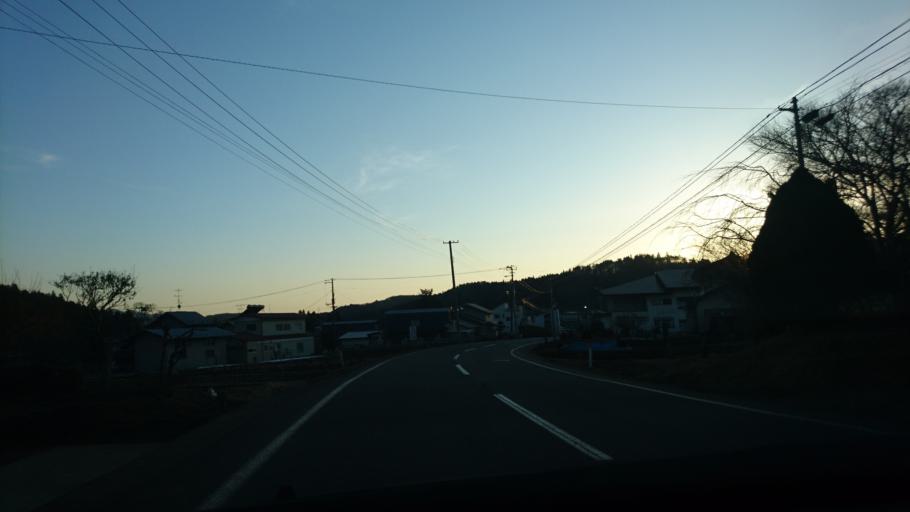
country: JP
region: Iwate
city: Mizusawa
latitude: 39.0351
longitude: 141.2970
